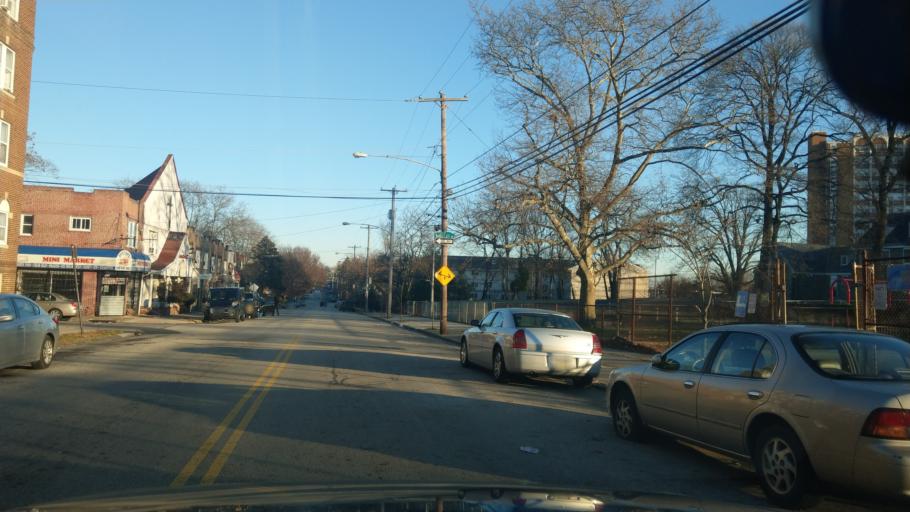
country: US
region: Pennsylvania
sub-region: Montgomery County
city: Wyncote
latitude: 40.0511
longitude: -75.1467
